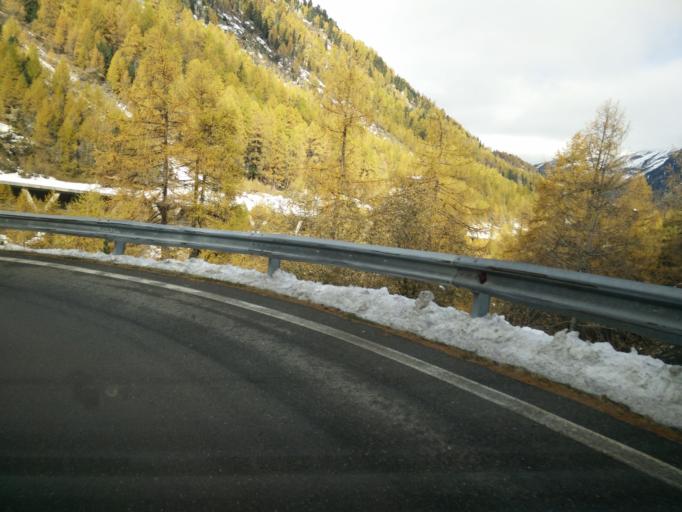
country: AT
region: Tyrol
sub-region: Politischer Bezirk Imst
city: Soelden
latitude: 46.9036
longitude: 11.0409
